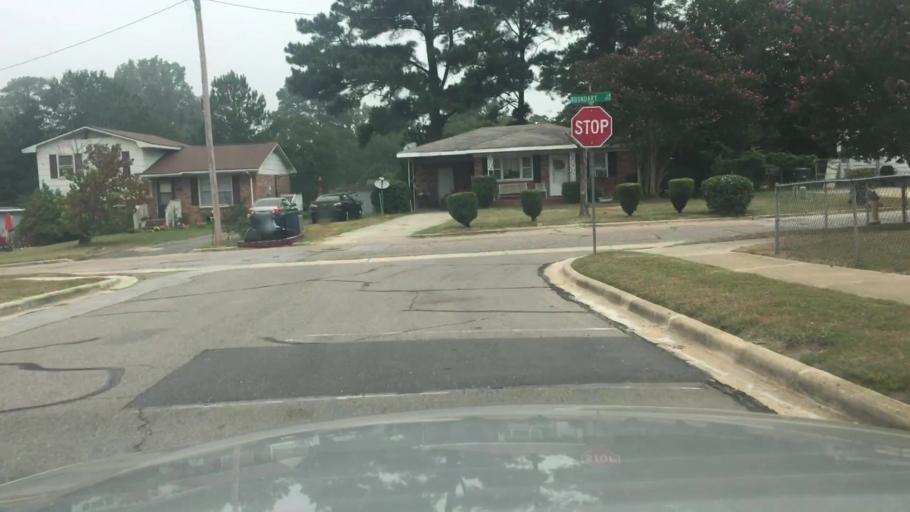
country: US
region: North Carolina
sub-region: Cumberland County
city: Fayetteville
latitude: 35.0704
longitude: -78.8859
